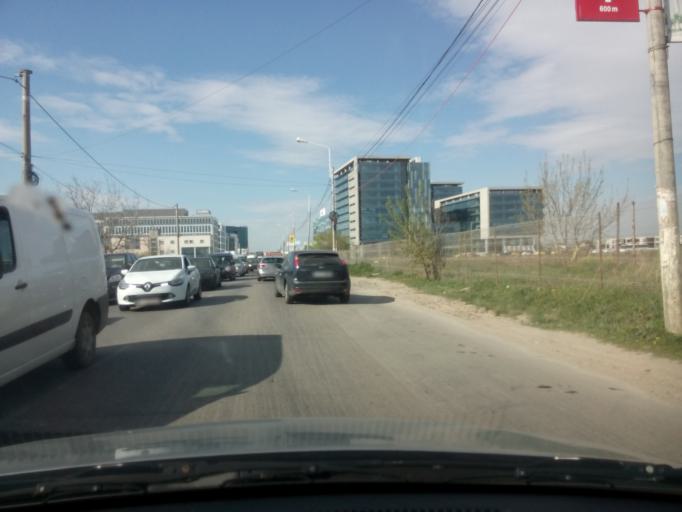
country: RO
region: Ilfov
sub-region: Voluntari City
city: Voluntari
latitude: 44.4863
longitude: 26.1262
